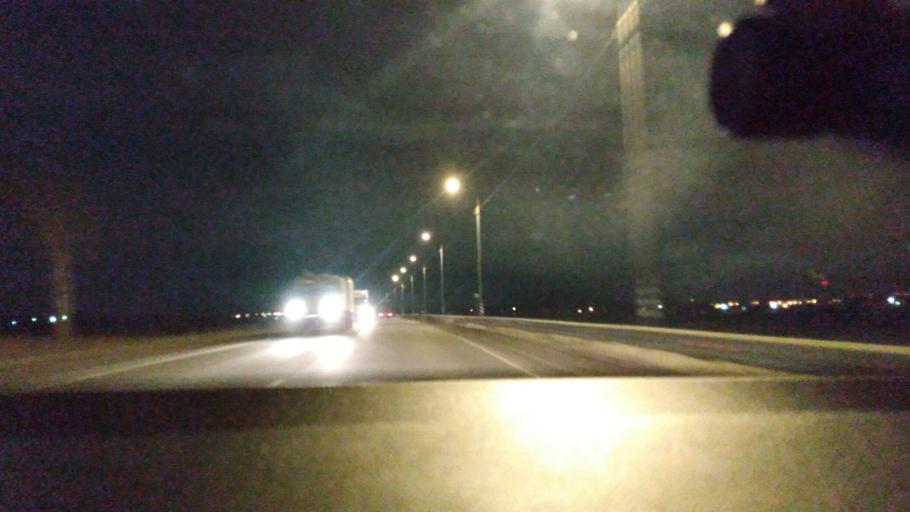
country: RU
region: Moskovskaya
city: Yegor'yevsk
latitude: 55.3987
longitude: 39.0625
